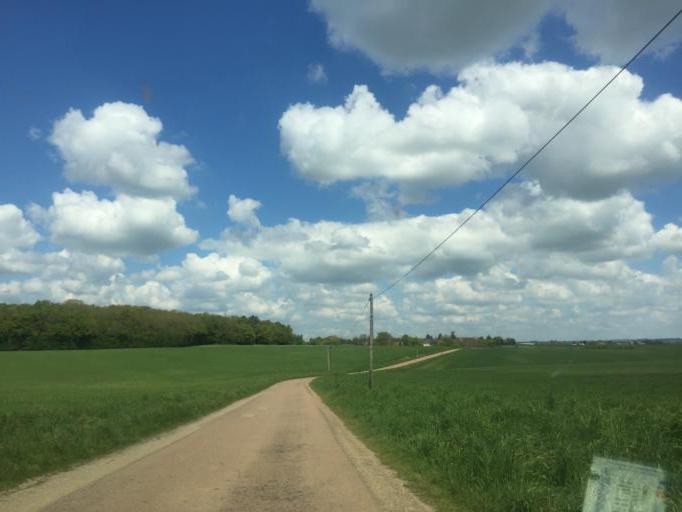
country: FR
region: Bourgogne
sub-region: Departement de l'Yonne
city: Fontenailles
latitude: 47.5195
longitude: 3.3464
